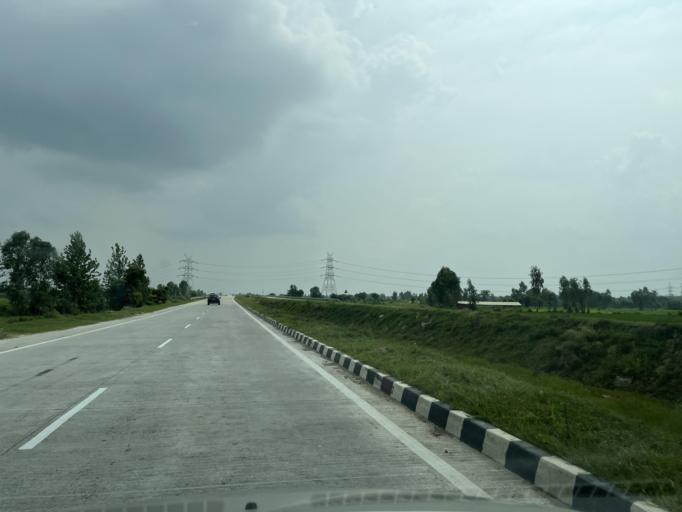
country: IN
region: Uttarakhand
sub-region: Udham Singh Nagar
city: Jaspur
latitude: 29.2760
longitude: 78.8681
